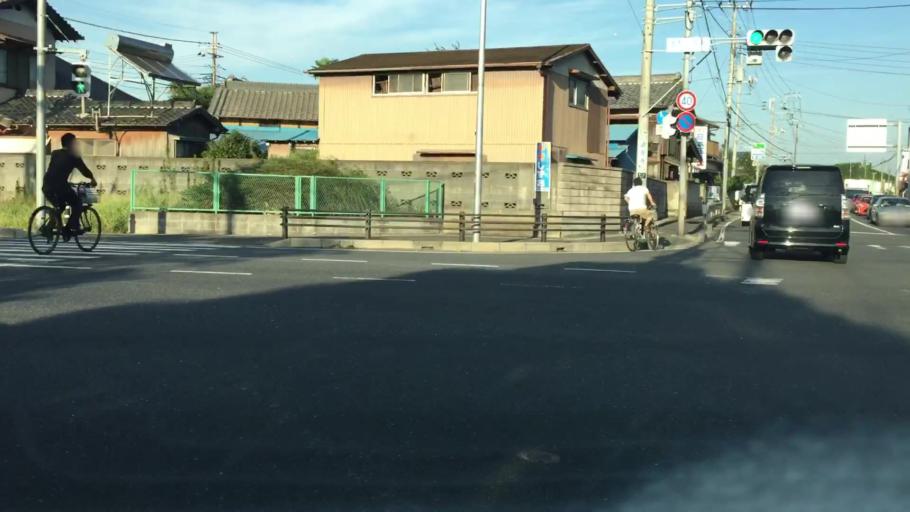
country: JP
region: Chiba
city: Funabashi
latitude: 35.7307
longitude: 140.0024
